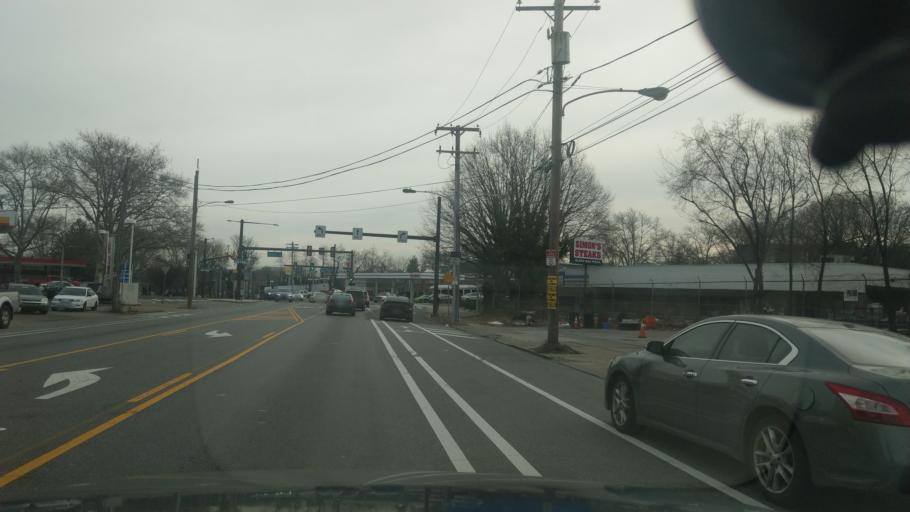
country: US
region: Pennsylvania
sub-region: Montgomery County
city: Wyncote
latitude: 40.0480
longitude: -75.1439
